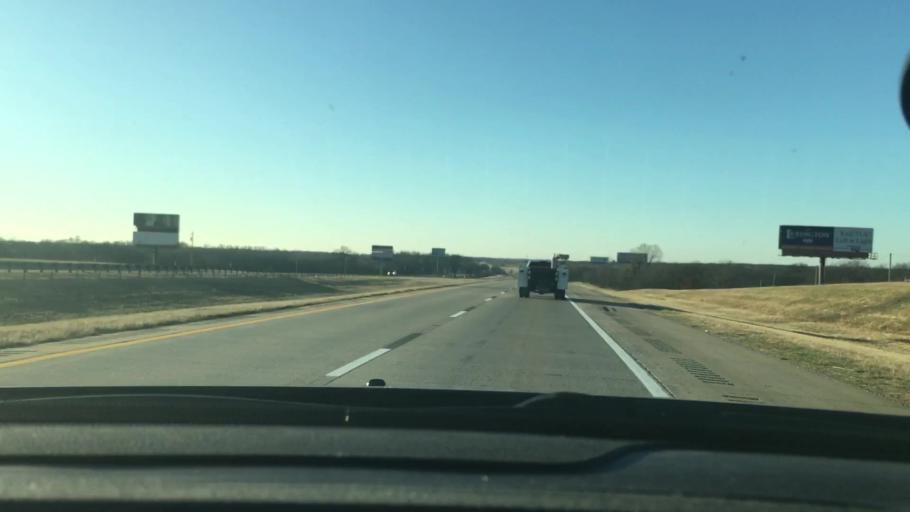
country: US
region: Oklahoma
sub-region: Carter County
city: Ardmore
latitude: 34.2747
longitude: -97.1621
